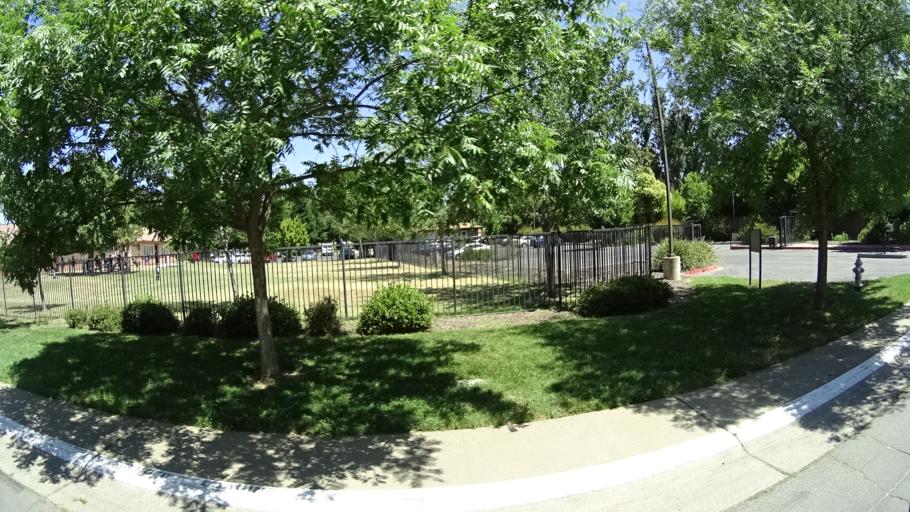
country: US
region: California
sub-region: Sacramento County
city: Parkway
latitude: 38.5380
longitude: -121.4774
